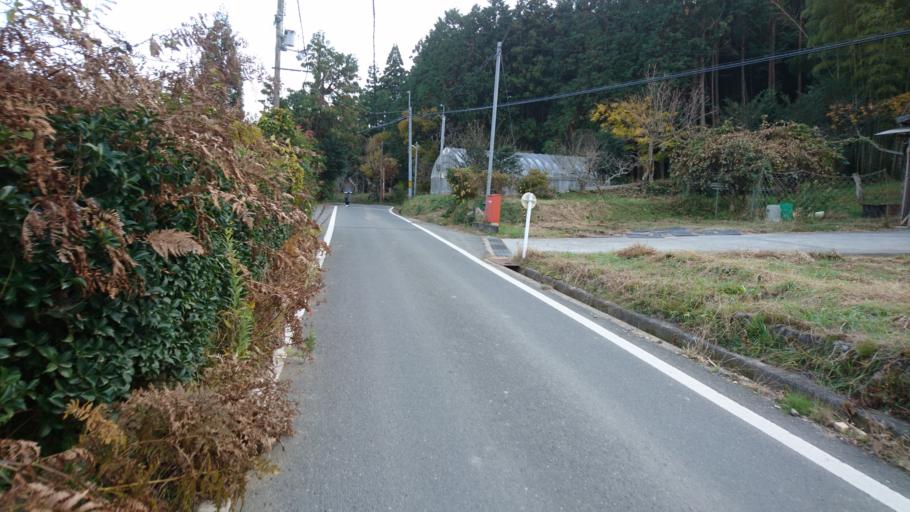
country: JP
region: Kyoto
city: Kameoka
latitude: 35.0442
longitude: 135.4740
